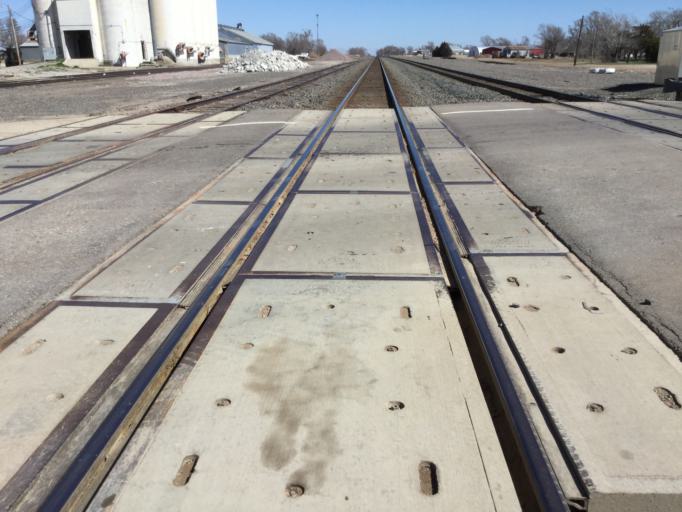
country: US
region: Kansas
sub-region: Barber County
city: Kiowa
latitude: 37.0170
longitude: -98.4916
